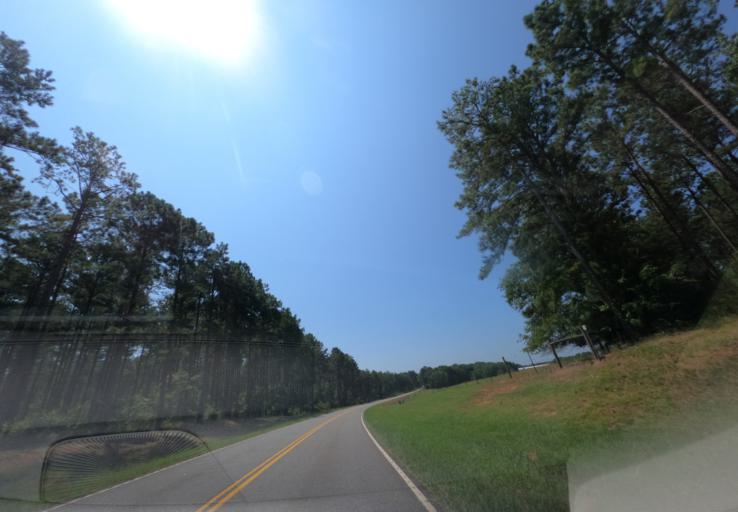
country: US
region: South Carolina
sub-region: McCormick County
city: McCormick
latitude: 33.9881
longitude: -82.1301
